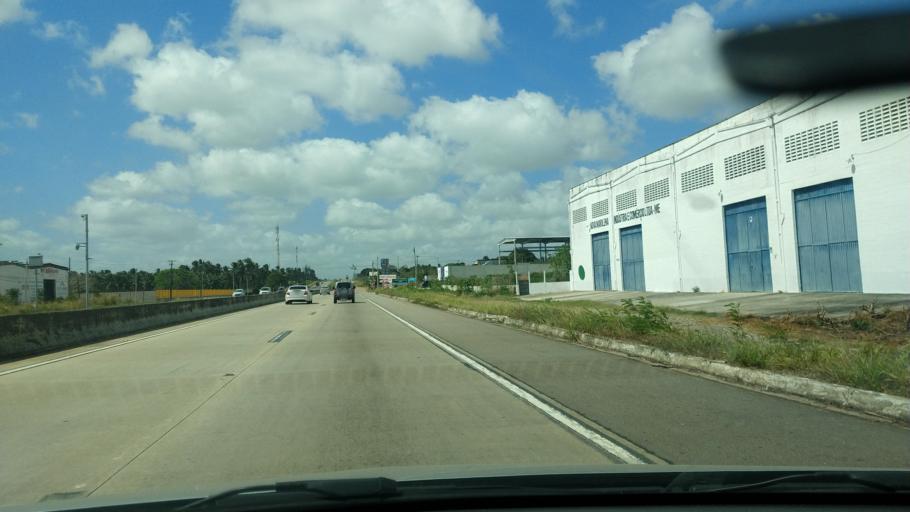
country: BR
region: Rio Grande do Norte
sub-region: Parnamirim
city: Parnamirim
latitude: -5.9520
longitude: -35.2647
